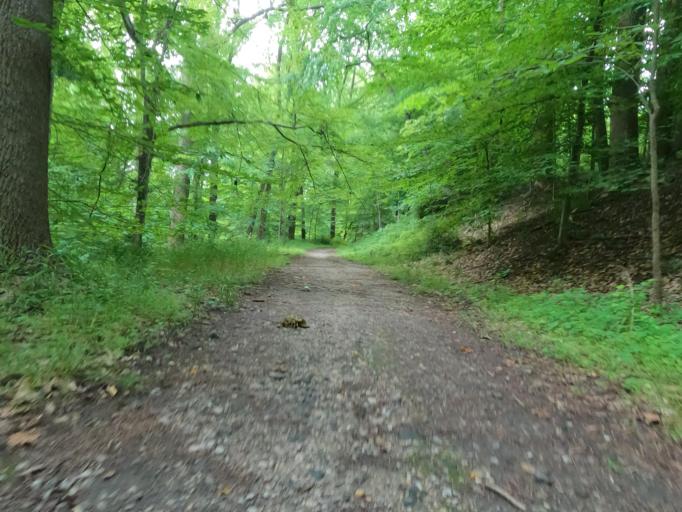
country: US
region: Maryland
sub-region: Howard County
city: Ellicott City
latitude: 39.2815
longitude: -76.7901
